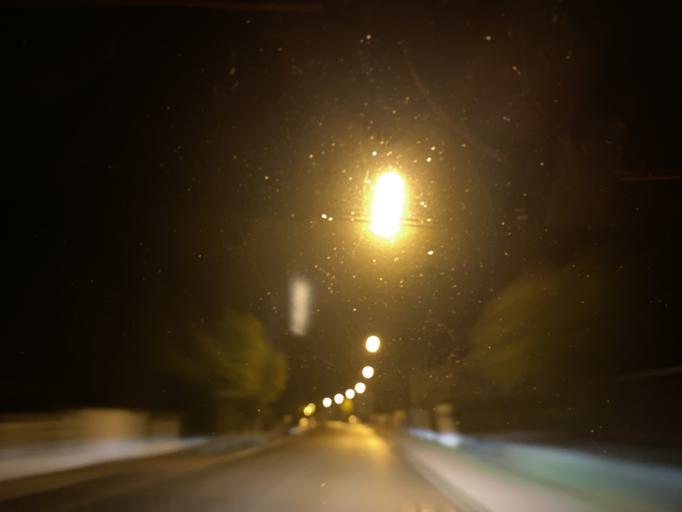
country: FR
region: Auvergne
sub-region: Departement de l'Allier
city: Abrest
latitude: 46.1045
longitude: 3.4402
